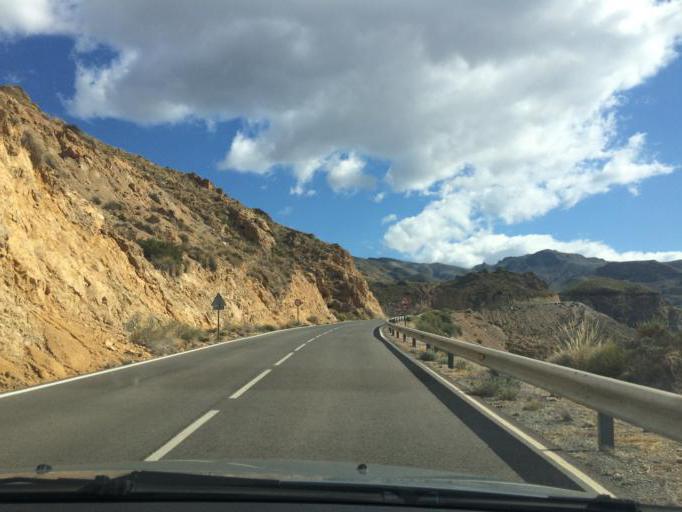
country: ES
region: Andalusia
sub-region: Provincia de Almeria
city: Pechina
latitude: 36.9539
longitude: -2.4096
